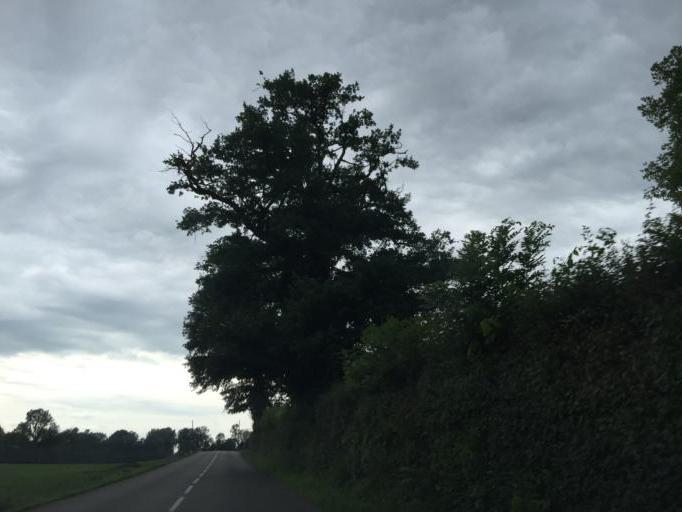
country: FR
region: Rhone-Alpes
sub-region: Departement de la Savoie
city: Le Pont-de-Beauvoisin
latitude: 45.5603
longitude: 5.6759
